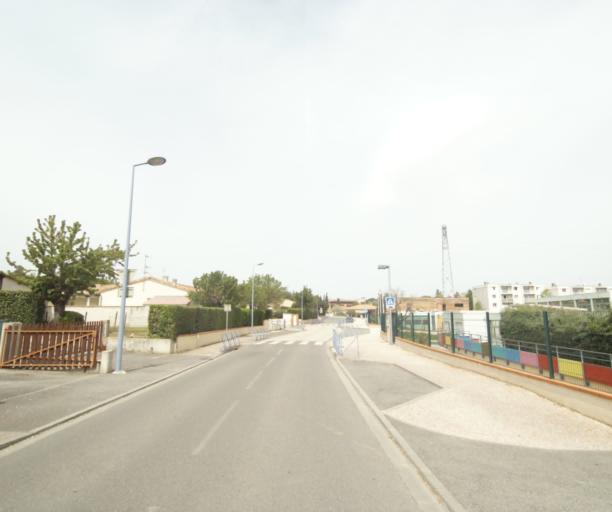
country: FR
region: Midi-Pyrenees
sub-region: Departement de la Haute-Garonne
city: Castanet-Tolosan
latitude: 43.5185
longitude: 1.4951
